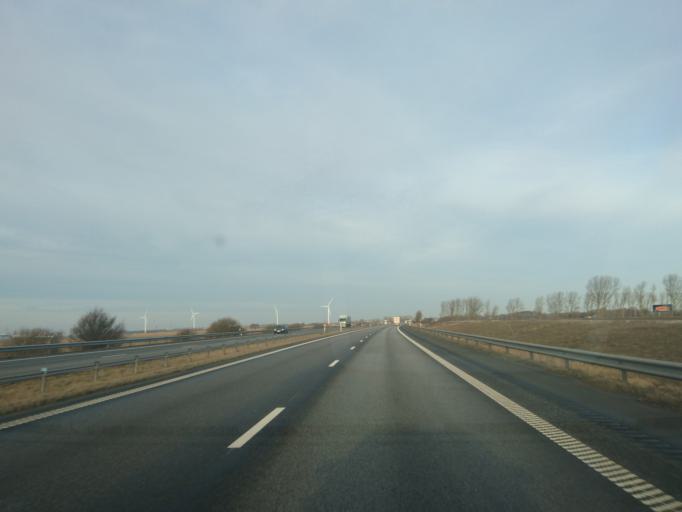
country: SE
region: Skane
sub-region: Landskrona
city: Asmundtorp
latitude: 55.8469
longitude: 12.9050
